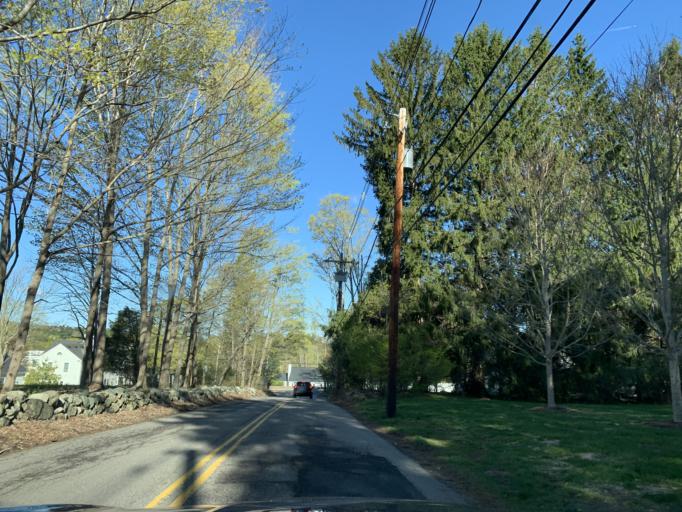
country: US
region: Massachusetts
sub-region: Norfolk County
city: Westwood
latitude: 42.2329
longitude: -71.2179
